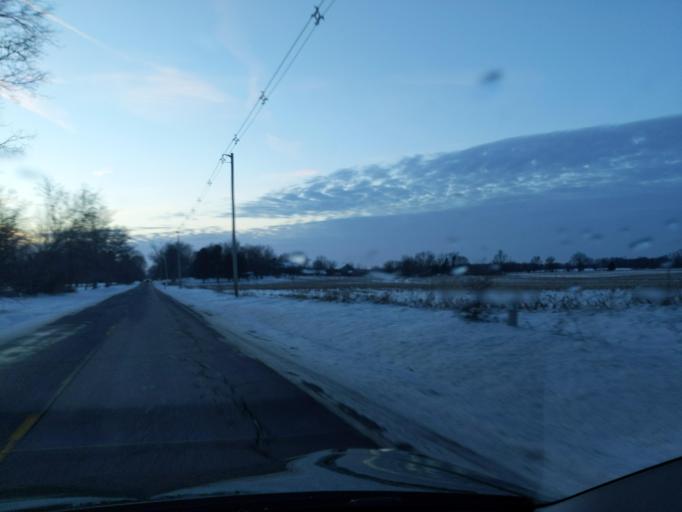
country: US
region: Michigan
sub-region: Ingham County
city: Mason
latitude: 42.5818
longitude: -84.3689
